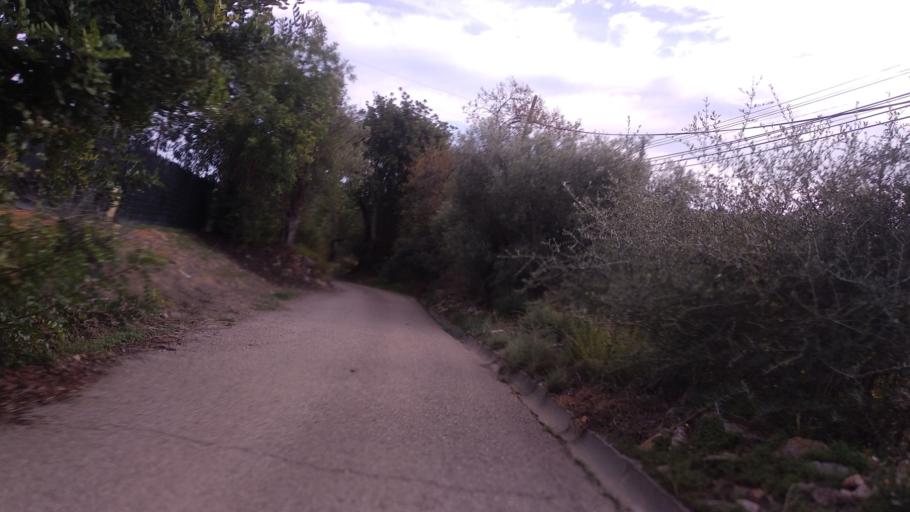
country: PT
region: Faro
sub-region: Sao Bras de Alportel
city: Sao Bras de Alportel
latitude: 37.1576
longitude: -7.8990
